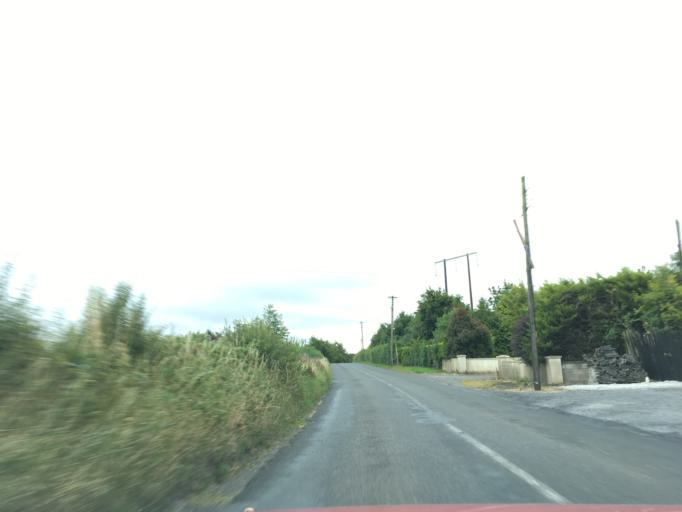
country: IE
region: Munster
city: Cashel
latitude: 52.4584
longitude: -7.8208
